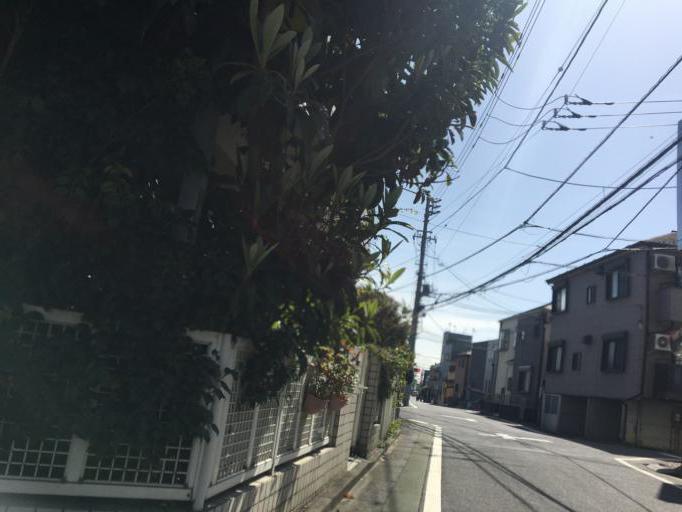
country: JP
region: Saitama
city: Wako
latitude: 35.7534
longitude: 139.6299
